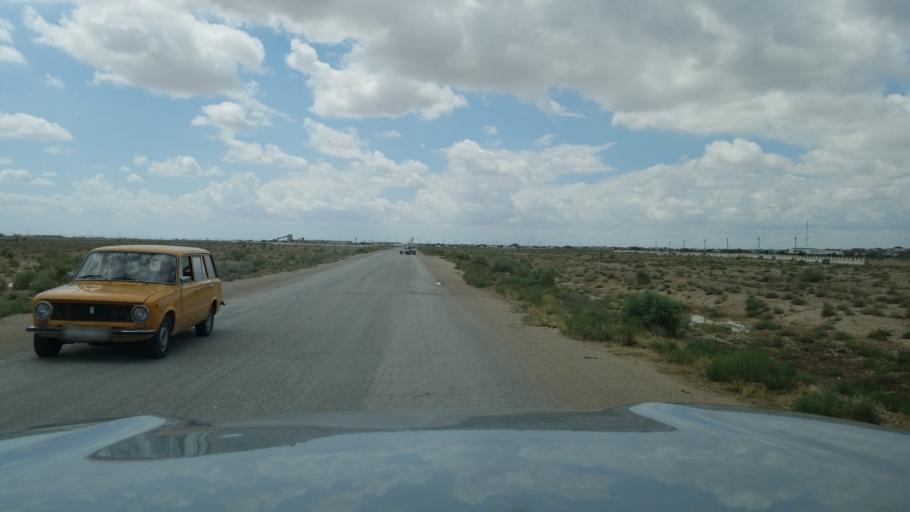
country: TM
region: Balkan
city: Balkanabat
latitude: 39.4887
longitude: 54.4058
